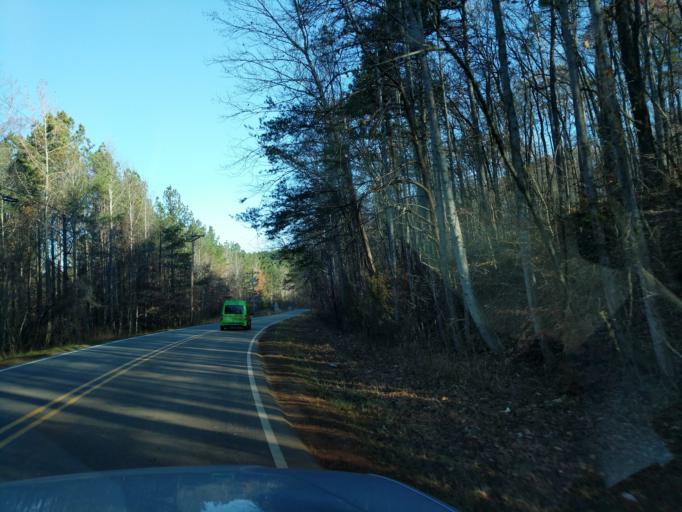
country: US
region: North Carolina
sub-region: Rutherford County
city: Rutherfordton
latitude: 35.2755
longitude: -82.0346
